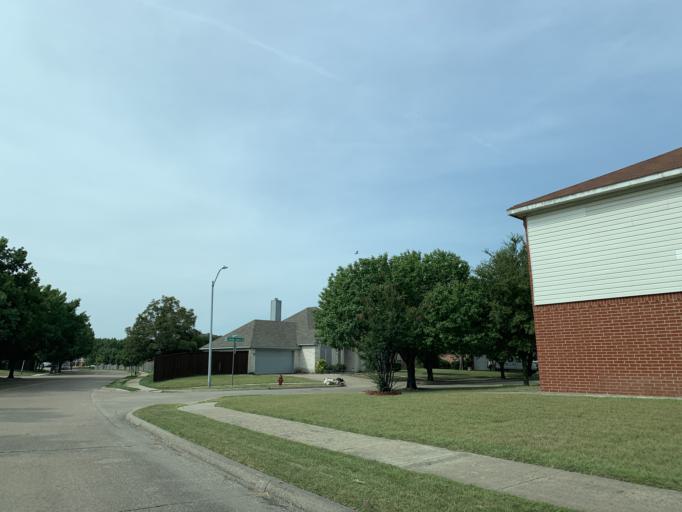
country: US
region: Texas
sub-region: Dallas County
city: Grand Prairie
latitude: 32.6604
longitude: -97.0096
